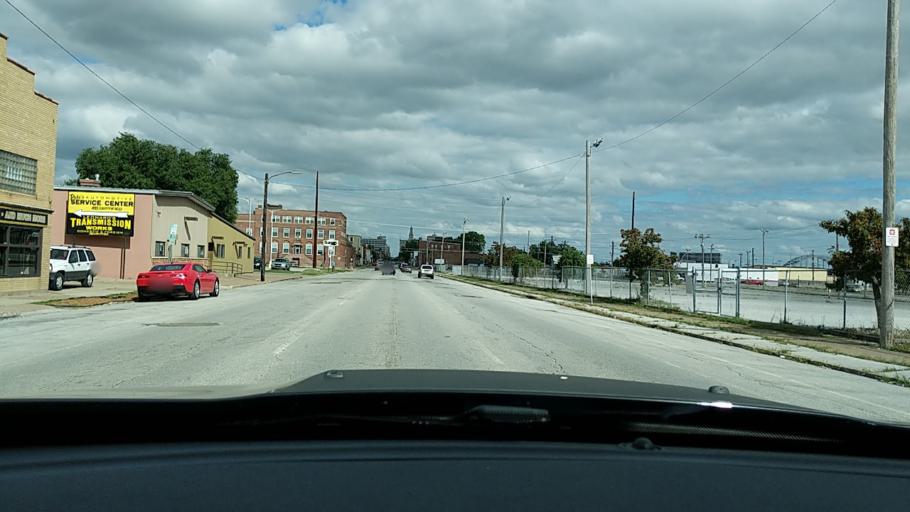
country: US
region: Iowa
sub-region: Scott County
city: Davenport
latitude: 41.5224
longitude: -90.5939
